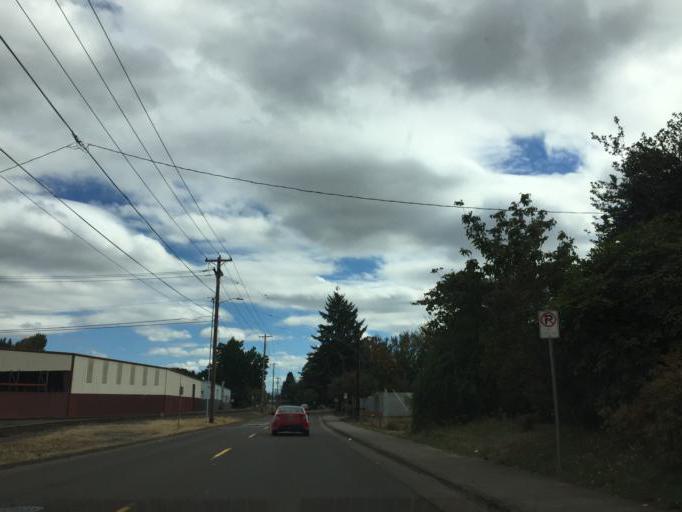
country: US
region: Oregon
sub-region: Marion County
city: Woodburn
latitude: 45.1407
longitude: -122.8572
